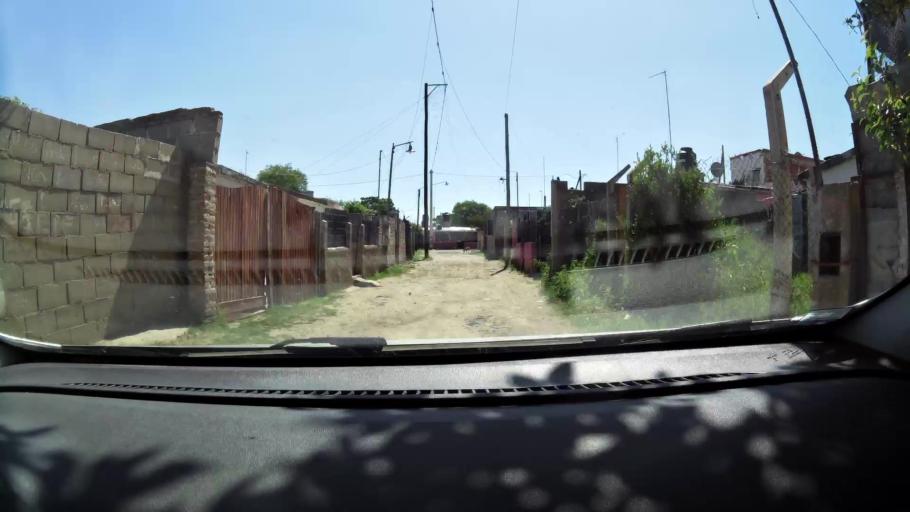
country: AR
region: Cordoba
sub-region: Departamento de Capital
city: Cordoba
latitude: -31.3640
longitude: -64.1420
